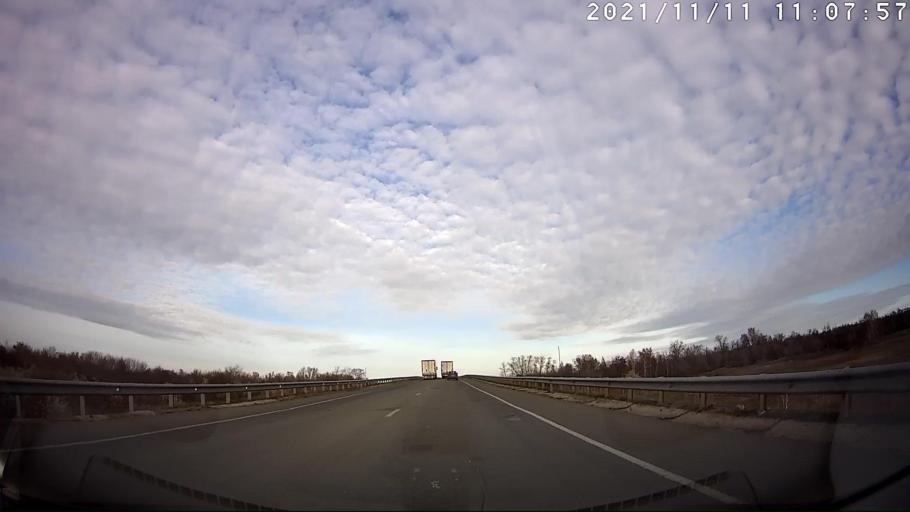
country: RU
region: Samara
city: Varlamovo
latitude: 53.1629
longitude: 48.2827
